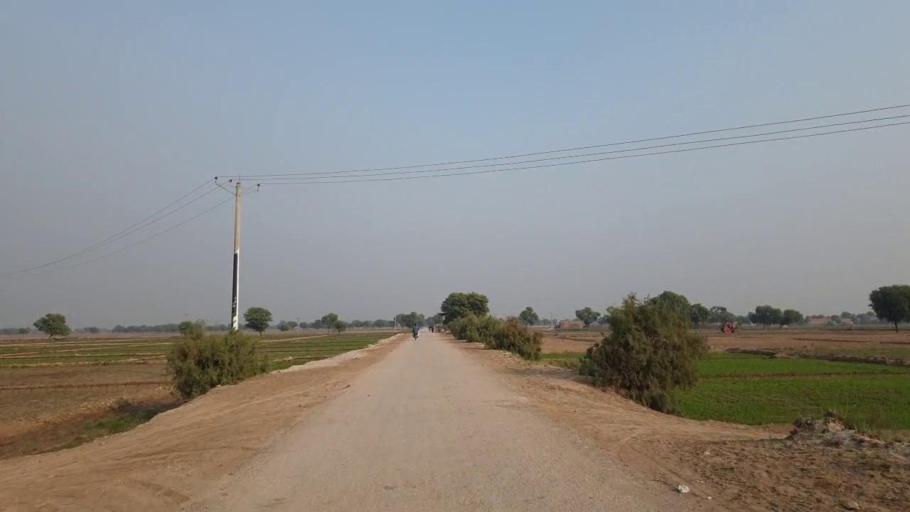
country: PK
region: Sindh
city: Bhan
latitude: 26.4960
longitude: 67.7319
